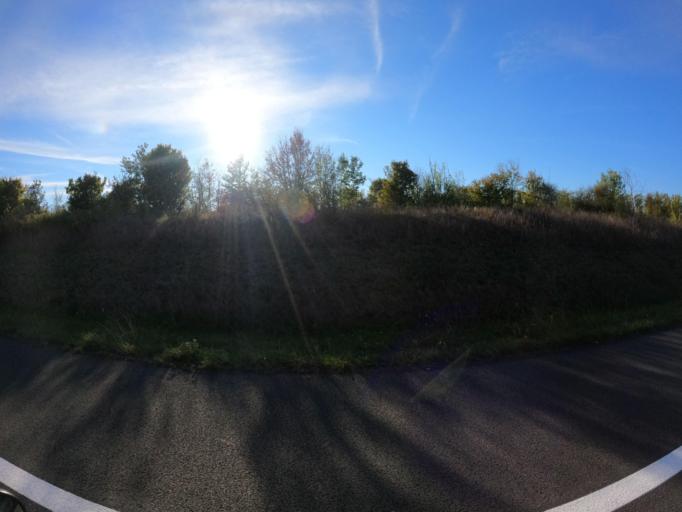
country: FR
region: Pays de la Loire
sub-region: Departement de Maine-et-Loire
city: Saint-Lambert-du-Lattay
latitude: 47.2733
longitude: -0.6149
